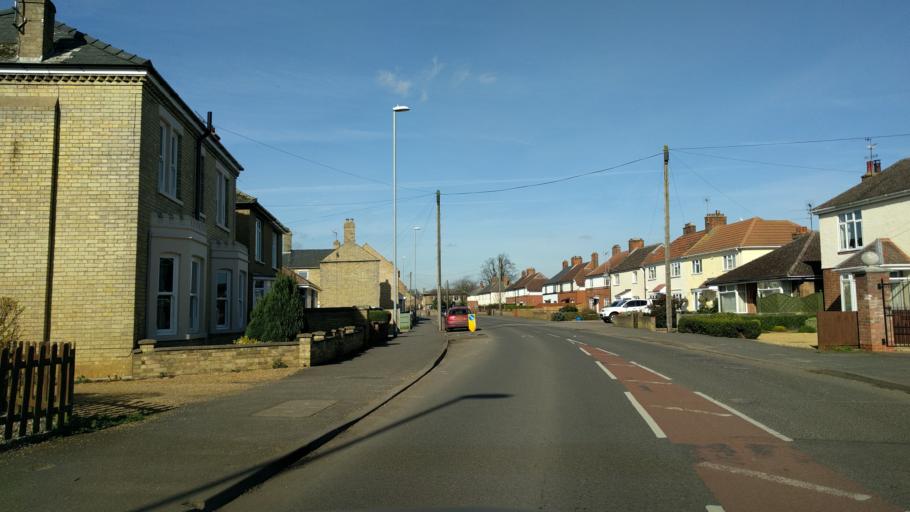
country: GB
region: England
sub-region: Cambridgeshire
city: Chatteris
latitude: 52.4473
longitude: 0.0471
